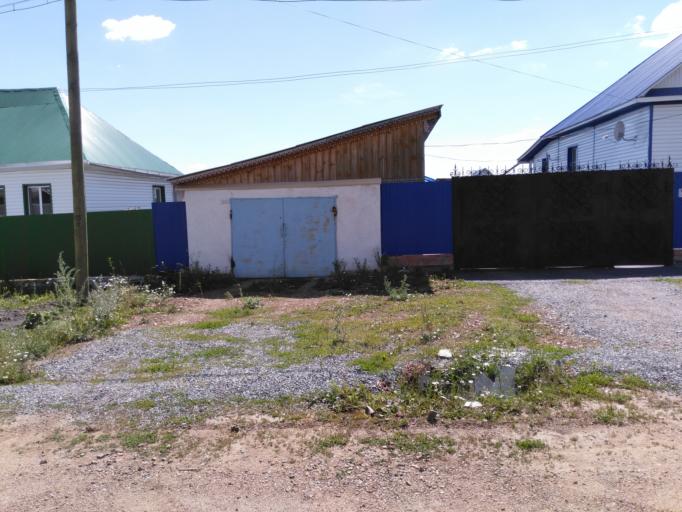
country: RU
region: Bashkortostan
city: Uchaly
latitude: 54.2906
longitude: 59.3617
